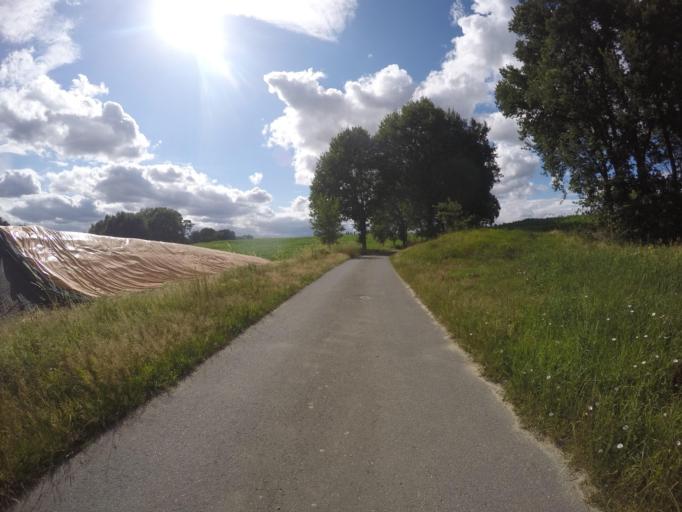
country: DE
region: Lower Saxony
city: Thomasburg
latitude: 53.2297
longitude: 10.6658
